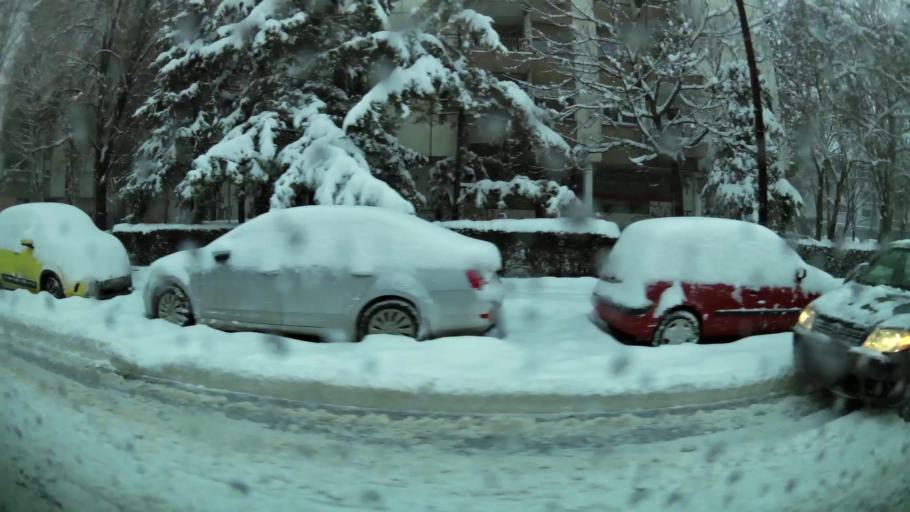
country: RS
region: Central Serbia
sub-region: Belgrade
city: Stari Grad
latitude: 44.8266
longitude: 20.4622
